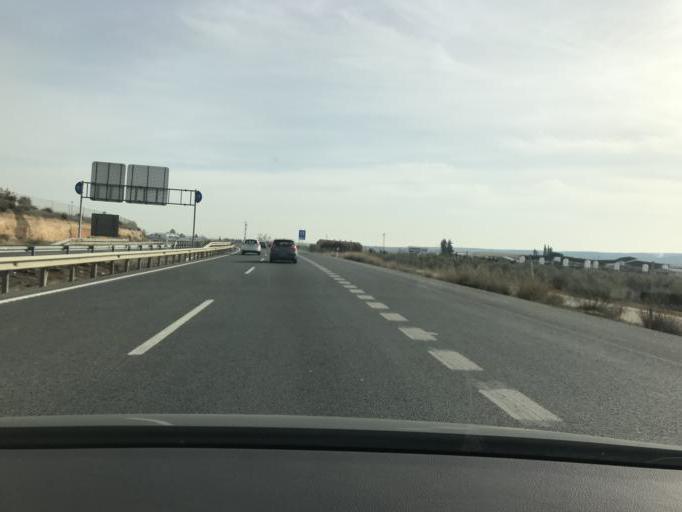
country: ES
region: Andalusia
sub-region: Provincia de Granada
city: Moraleda de Zafayona
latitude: 37.1803
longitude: -3.9446
